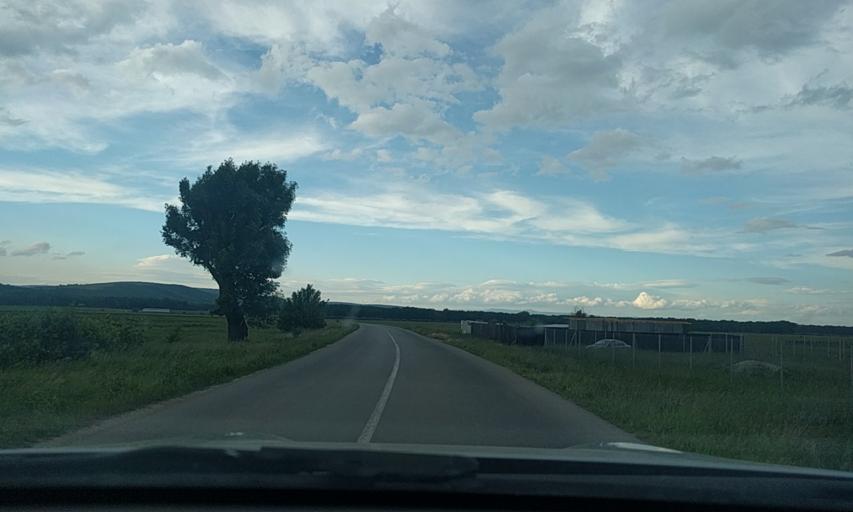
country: RO
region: Brasov
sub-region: Comuna Harman
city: Harman
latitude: 45.7350
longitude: 25.7025
